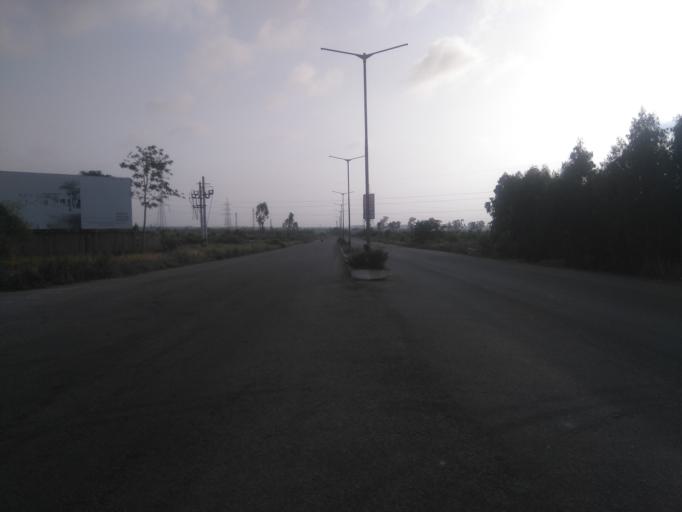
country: IN
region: Karnataka
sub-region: Bangalore Rural
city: Devanhalli
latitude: 13.1628
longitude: 77.6856
